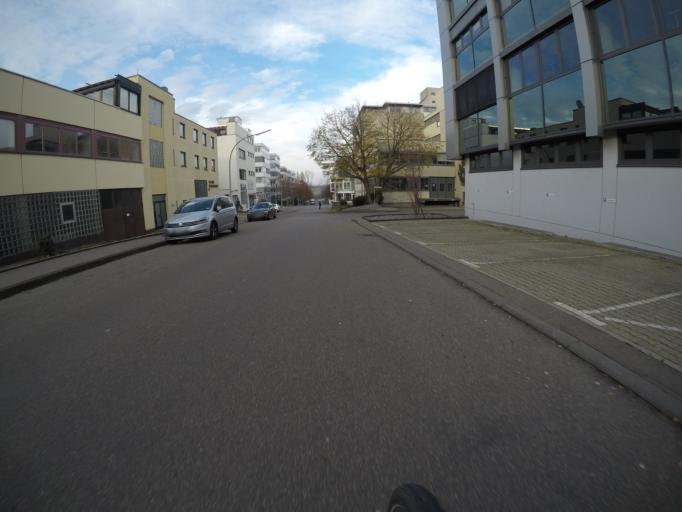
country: DE
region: Baden-Wuerttemberg
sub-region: Regierungsbezirk Stuttgart
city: Leinfelden-Echterdingen
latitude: 48.6954
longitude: 9.1633
